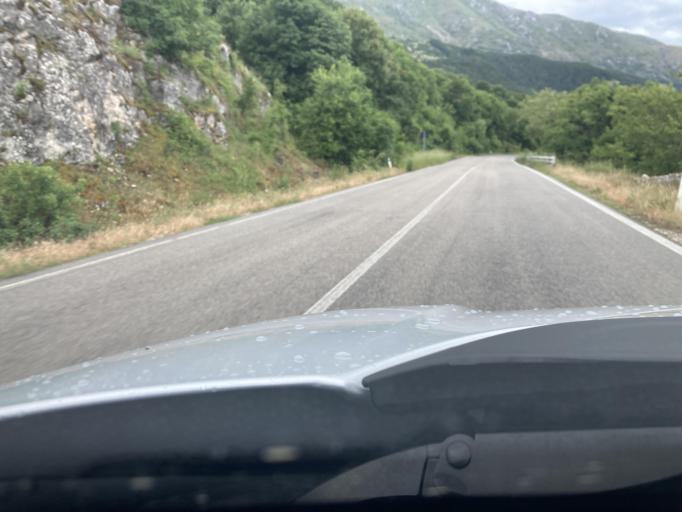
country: IT
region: Abruzzo
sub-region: Provincia dell' Aquila
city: San Panfilo d'Ocre
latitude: 42.2745
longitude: 13.4795
